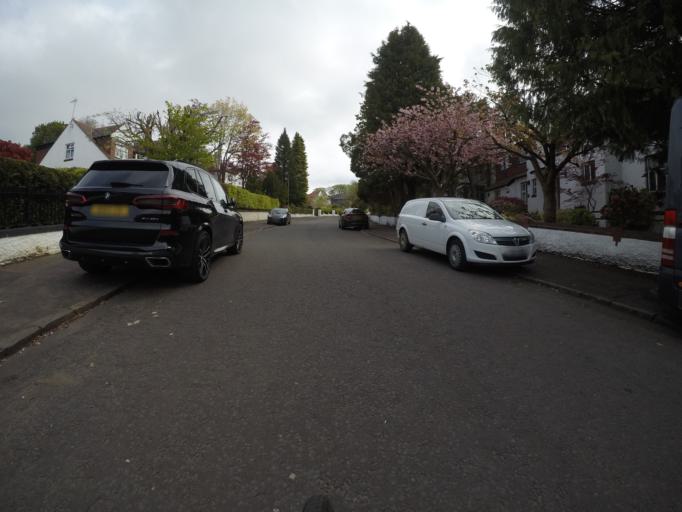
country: GB
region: Scotland
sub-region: East Renfrewshire
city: Giffnock
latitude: 55.7878
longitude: -4.3057
